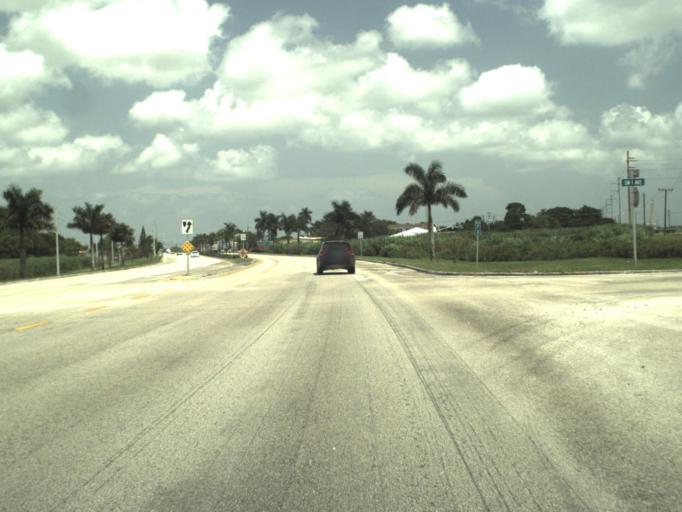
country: US
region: Florida
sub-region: Palm Beach County
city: South Bay
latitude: 26.6576
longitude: -80.7127
